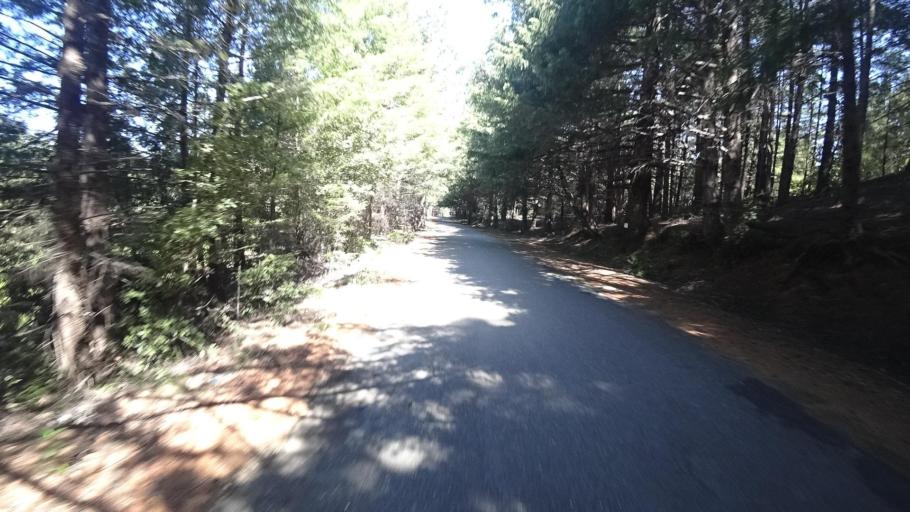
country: US
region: California
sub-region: Humboldt County
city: Redway
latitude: 40.1687
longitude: -124.0855
